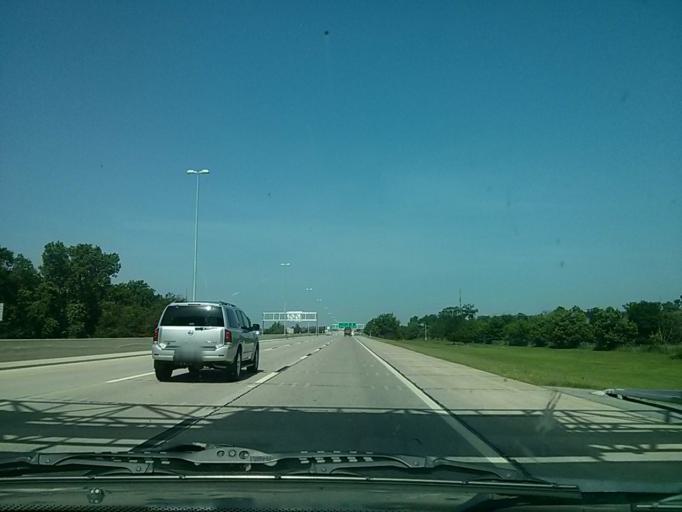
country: US
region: Oklahoma
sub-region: Tulsa County
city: Jenks
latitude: 36.0096
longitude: -95.9996
